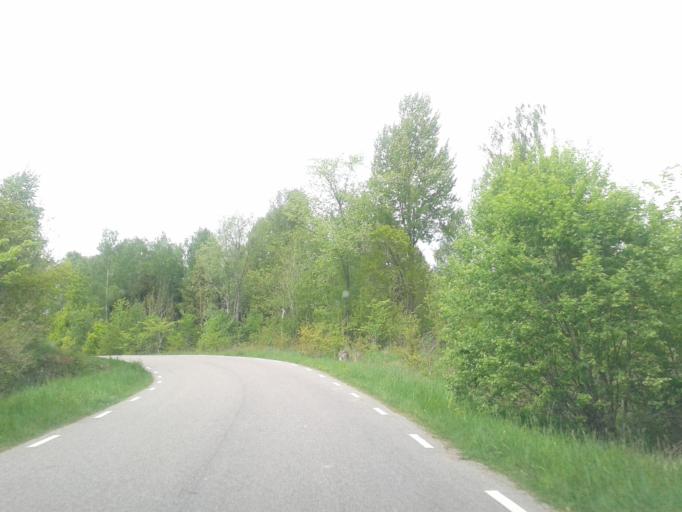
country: SE
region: Vaestra Goetaland
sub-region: Kungalvs Kommun
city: Kungalv
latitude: 57.8560
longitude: 11.9367
